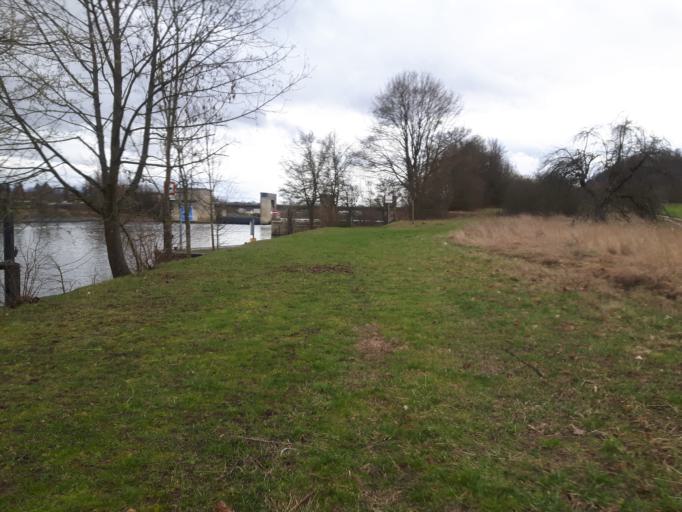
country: DE
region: Baden-Wuerttemberg
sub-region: Regierungsbezirk Stuttgart
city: Gundelsheim
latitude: 49.2839
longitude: 9.1541
